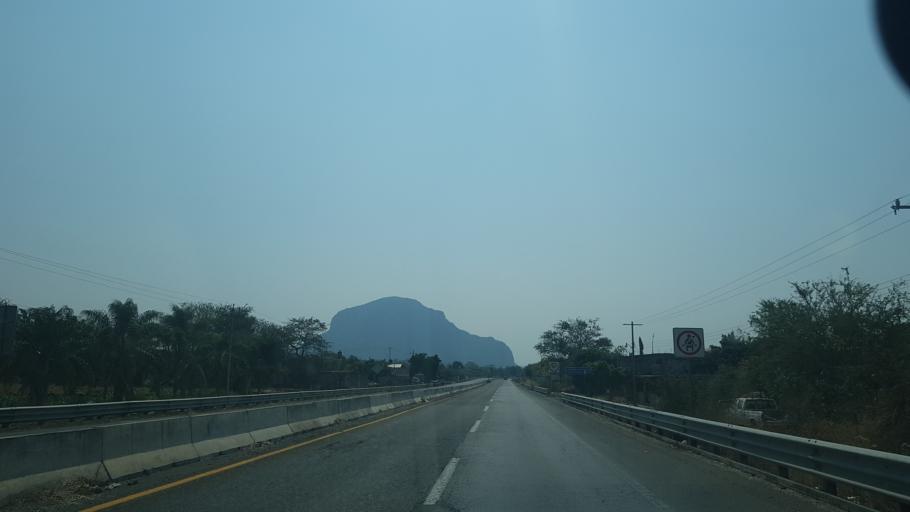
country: MX
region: Morelos
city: Amayuca
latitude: 18.7153
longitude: -98.7893
